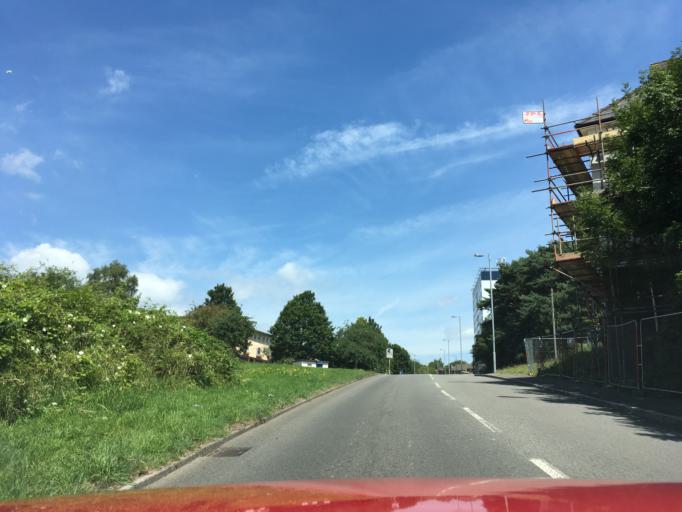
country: GB
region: Wales
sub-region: Newport
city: Newport
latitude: 51.5760
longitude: -3.0192
